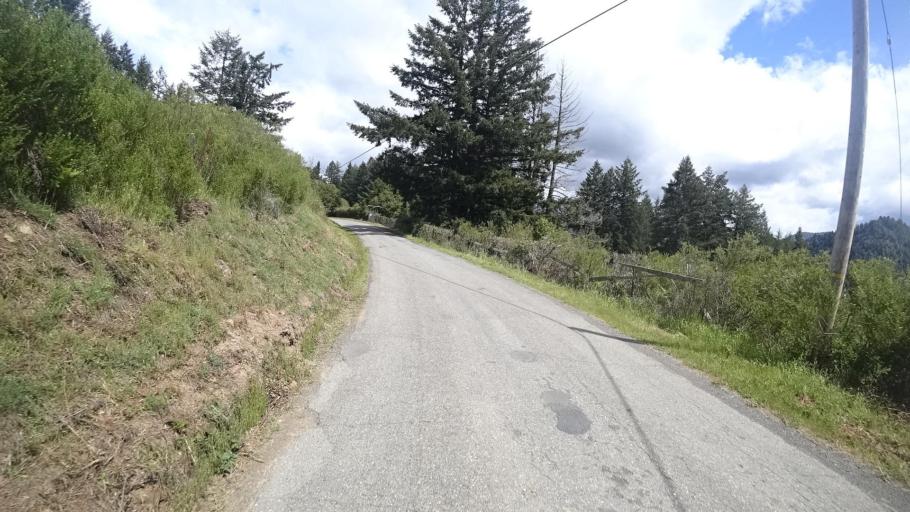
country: US
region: California
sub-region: Humboldt County
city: Blue Lake
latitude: 40.7653
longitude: -123.9423
